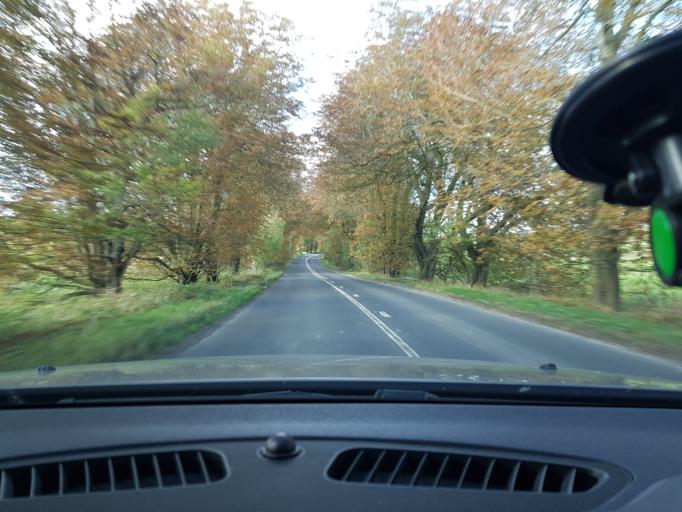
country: GB
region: England
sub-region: Borough of Swindon
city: Wanborough
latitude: 51.5148
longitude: -1.6801
